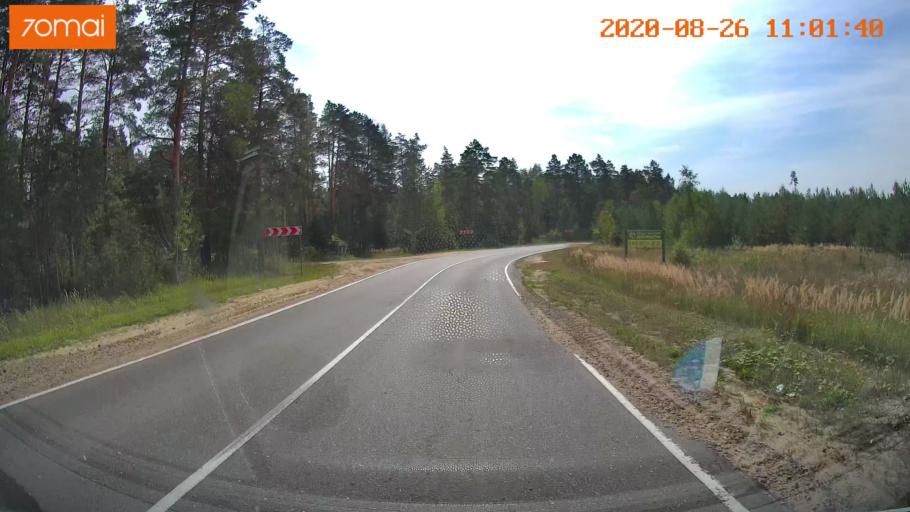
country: RU
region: Rjazan
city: Izhevskoye
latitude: 54.5602
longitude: 41.2270
